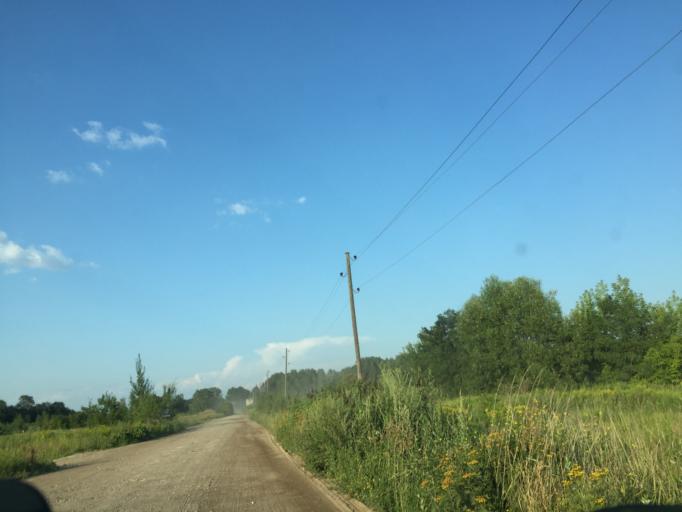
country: LV
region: Riga
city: Bergi
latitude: 56.9763
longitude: 24.3512
